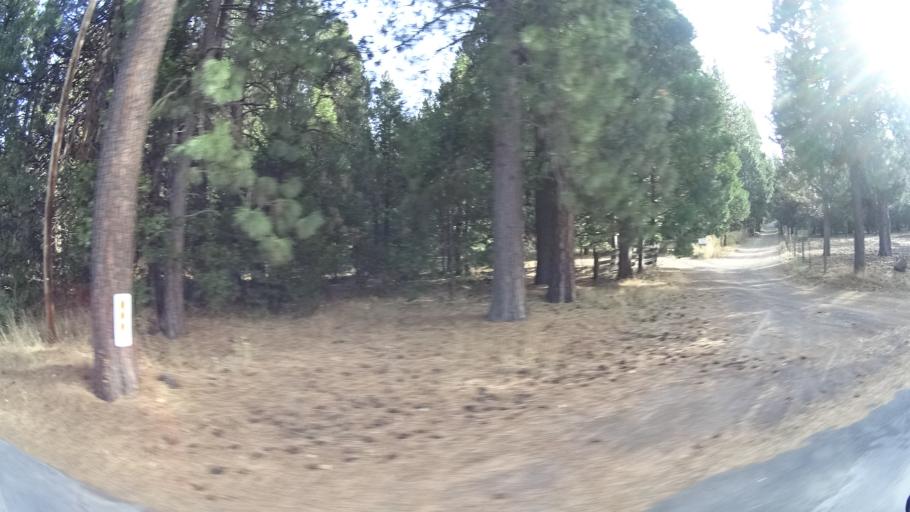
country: US
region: California
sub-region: Siskiyou County
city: Weed
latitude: 41.4471
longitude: -122.3796
